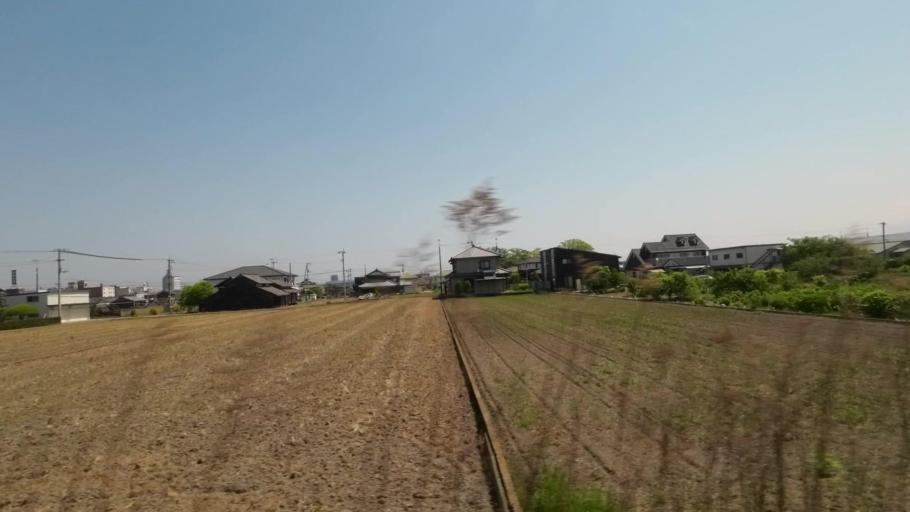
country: JP
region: Ehime
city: Saijo
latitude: 33.9257
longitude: 133.0891
